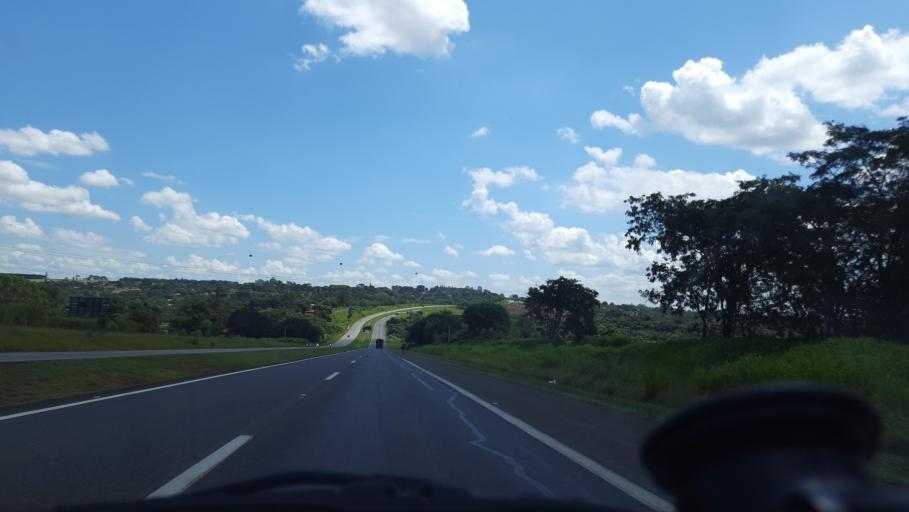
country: BR
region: Sao Paulo
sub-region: Moji-Guacu
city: Mogi-Gaucu
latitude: -22.2843
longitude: -46.9724
